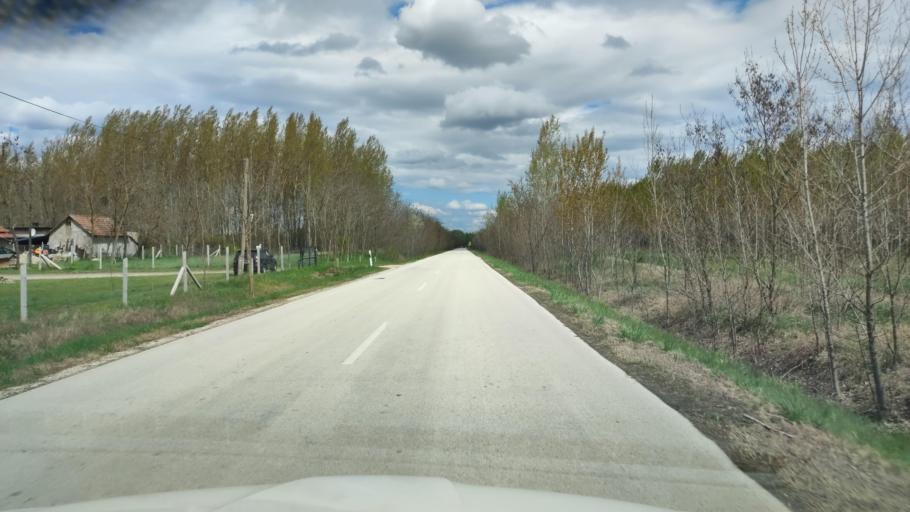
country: HU
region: Pest
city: Kocser
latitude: 47.0464
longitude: 19.9439
